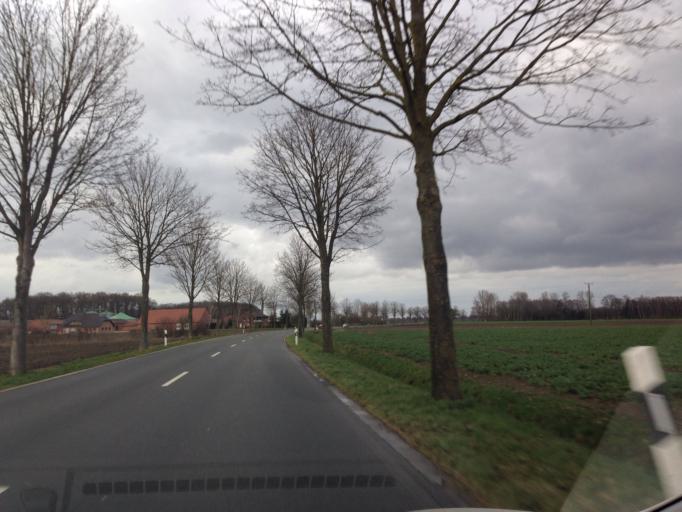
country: DE
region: North Rhine-Westphalia
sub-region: Regierungsbezirk Munster
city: Senden
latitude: 51.8008
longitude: 7.5364
